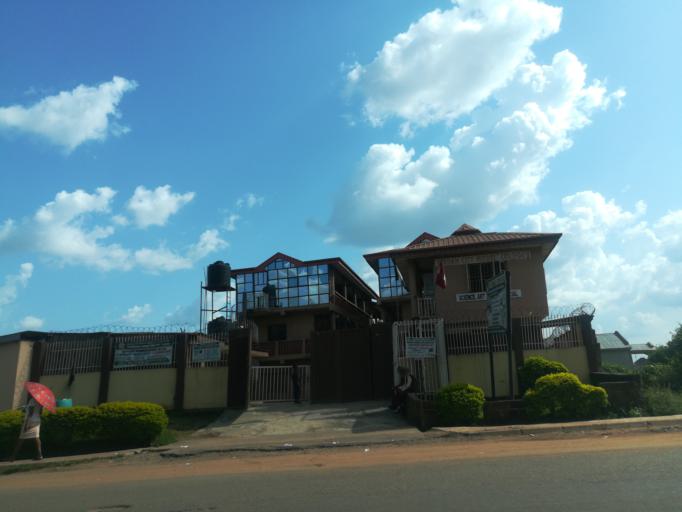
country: NG
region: Oyo
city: Ibadan
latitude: 7.4224
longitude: 3.9777
